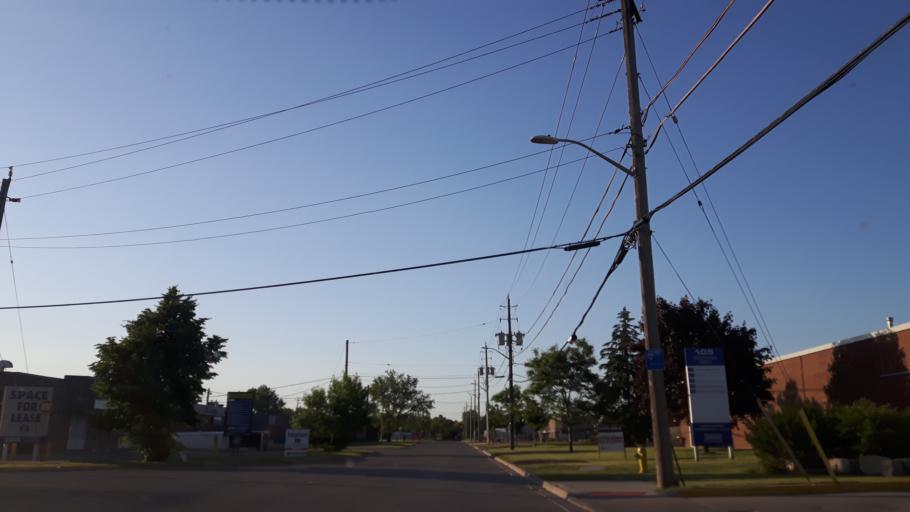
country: CA
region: Ontario
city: London
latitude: 42.9318
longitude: -81.2119
